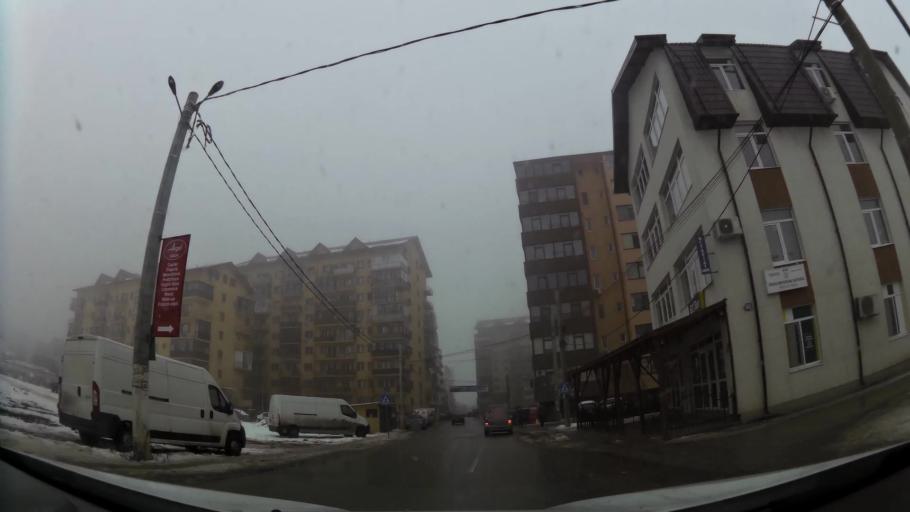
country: RO
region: Ilfov
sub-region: Comuna Chiajna
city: Chiajna
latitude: 44.4441
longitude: 25.9833
